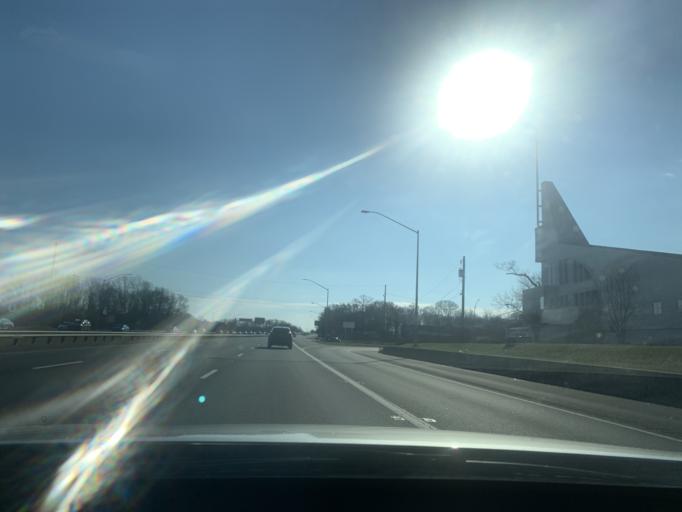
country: US
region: Maryland
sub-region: Prince George's County
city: Camp Springs
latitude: 38.8132
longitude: -76.9130
